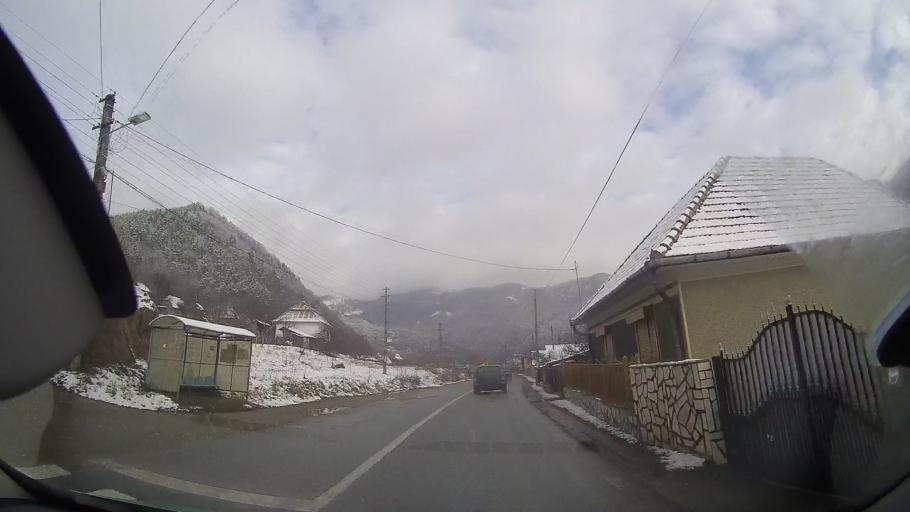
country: RO
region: Alba
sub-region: Oras Baia de Aries
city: Baia de Aries
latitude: 46.3982
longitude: 23.3189
